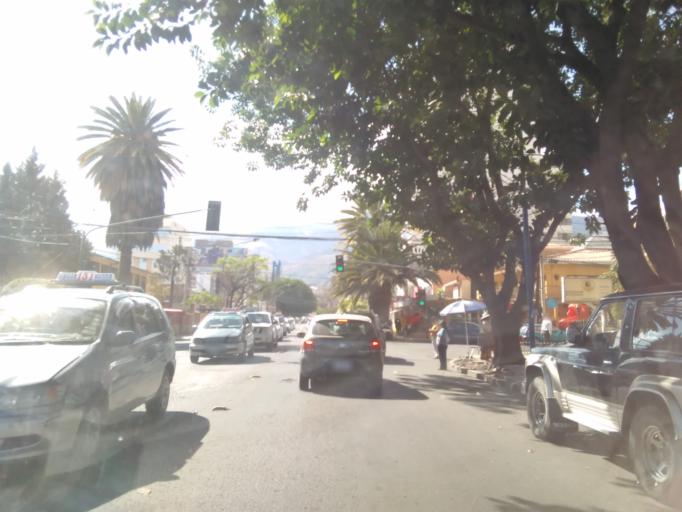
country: BO
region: Cochabamba
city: Cochabamba
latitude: -17.3773
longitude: -66.1569
